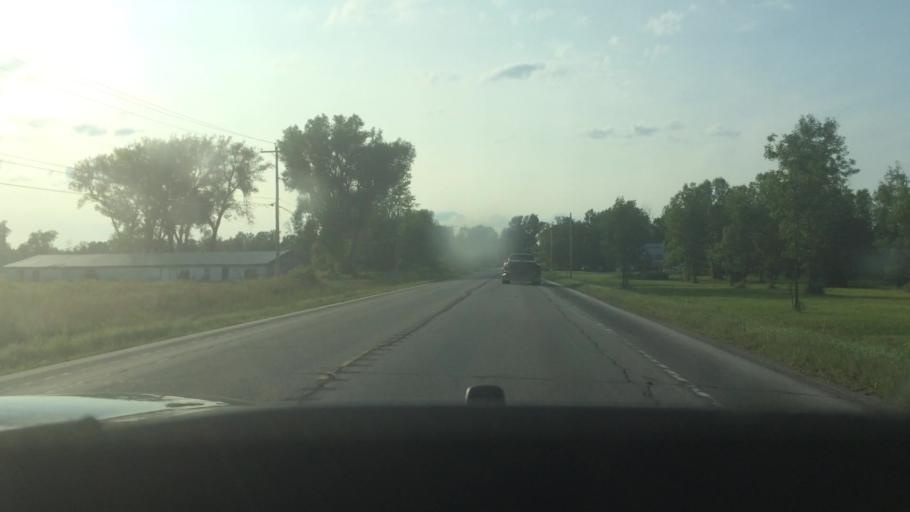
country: US
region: New York
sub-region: St. Lawrence County
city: Ogdensburg
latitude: 44.6745
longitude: -75.4340
